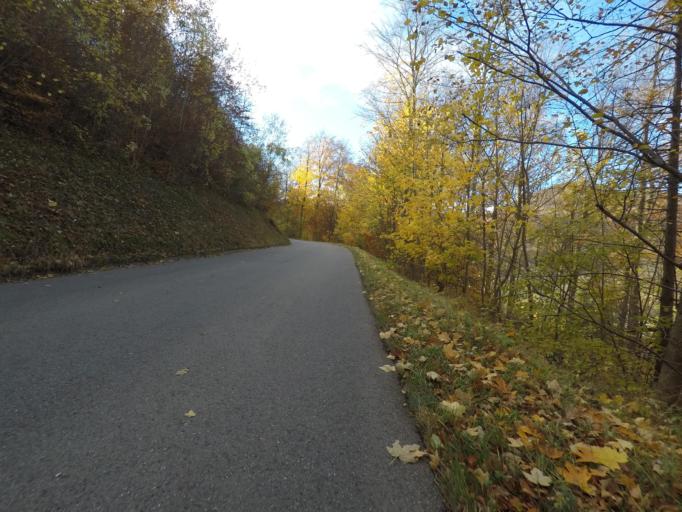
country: DE
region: Baden-Wuerttemberg
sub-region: Tuebingen Region
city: Pfullingen
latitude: 48.4247
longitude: 9.2461
